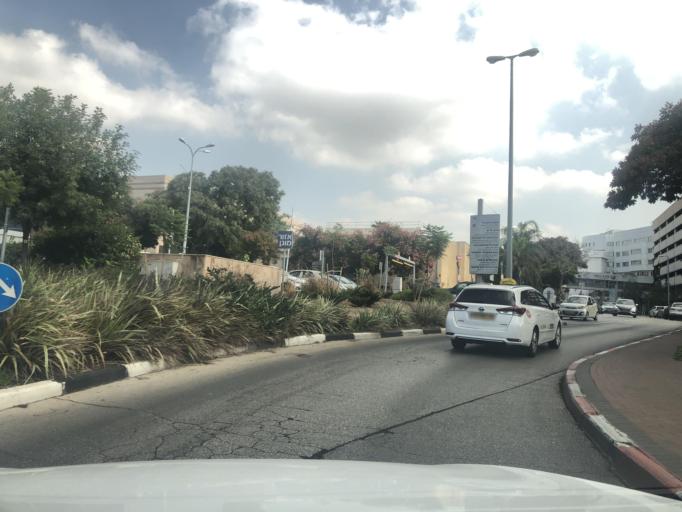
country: IL
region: Tel Aviv
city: Or Yehuda
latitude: 32.0482
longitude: 34.8409
